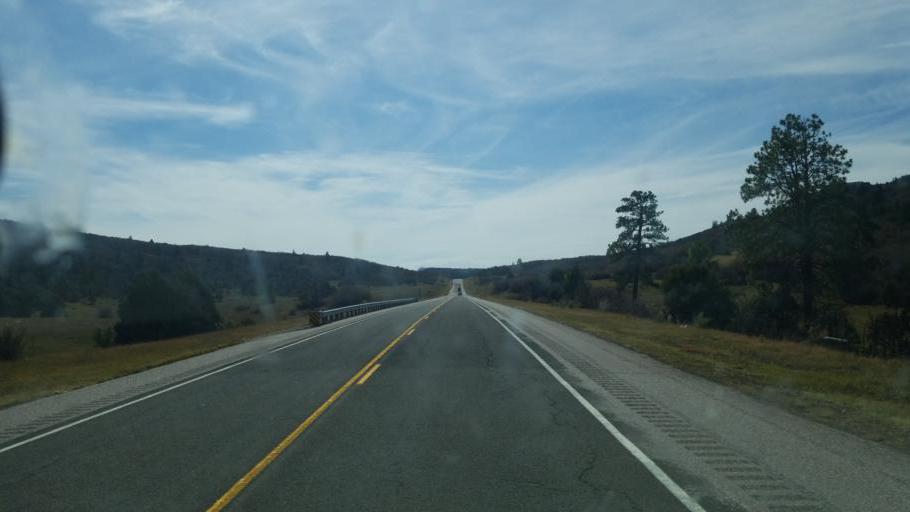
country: US
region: New Mexico
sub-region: Rio Arriba County
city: Chama
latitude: 36.9813
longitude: -106.7802
